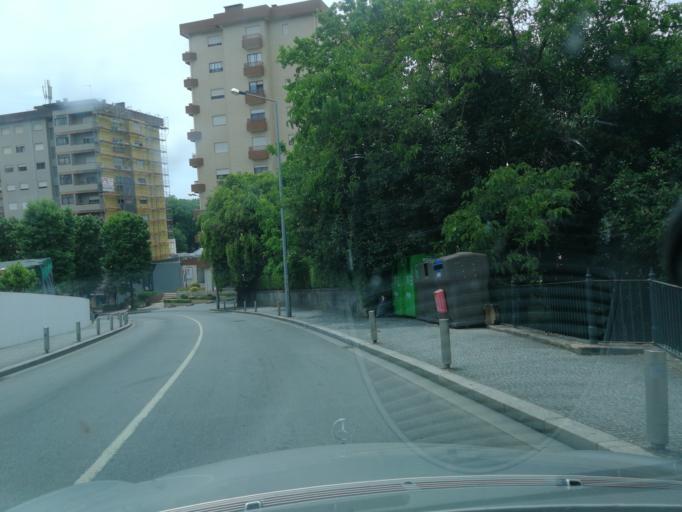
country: PT
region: Braga
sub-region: Vila Nova de Famalicao
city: Vila Nova de Famalicao
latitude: 41.4098
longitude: -8.5226
